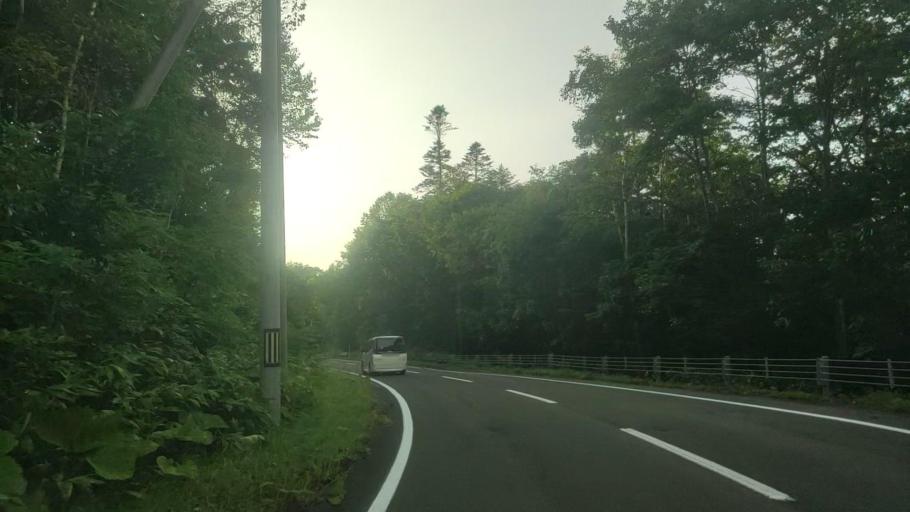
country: JP
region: Hokkaido
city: Bibai
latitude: 43.1713
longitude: 142.0732
